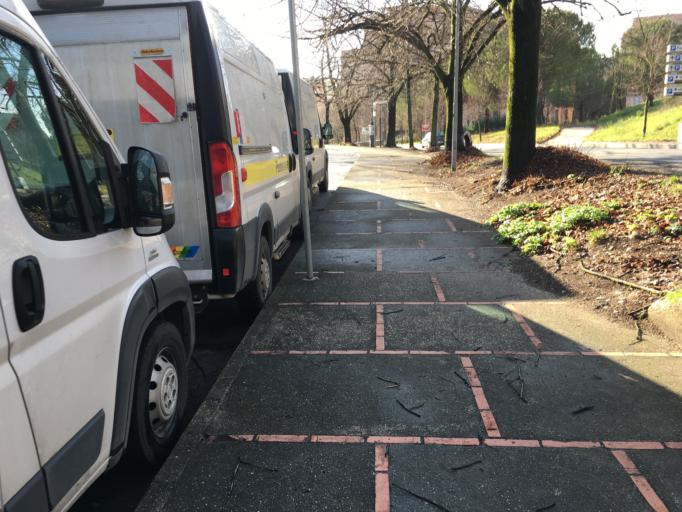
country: IT
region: Umbria
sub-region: Provincia di Perugia
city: Perugia
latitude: 43.1080
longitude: 12.3774
